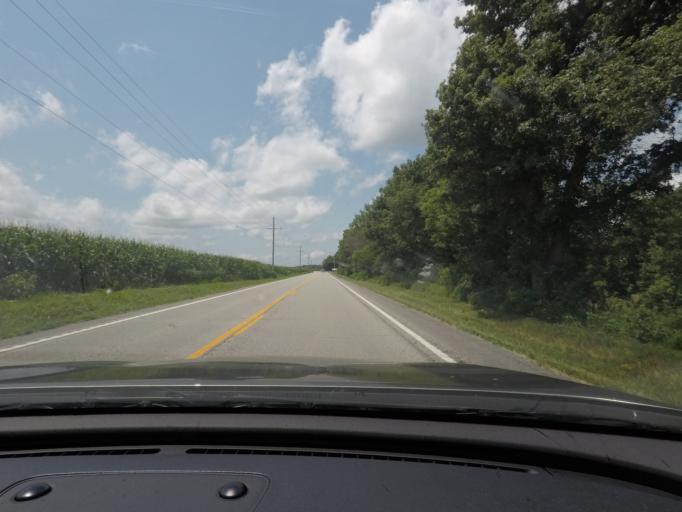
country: US
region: Missouri
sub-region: Carroll County
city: Carrollton
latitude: 39.1948
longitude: -93.4162
